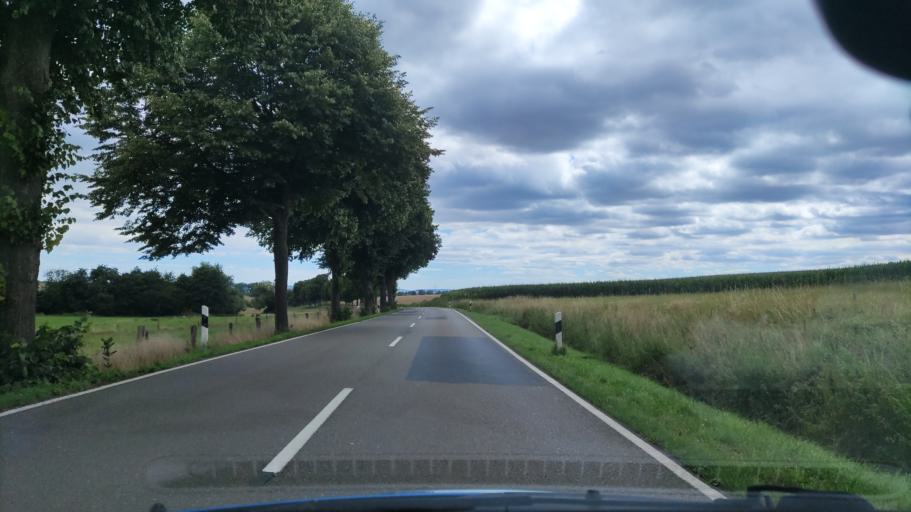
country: DE
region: Lower Saxony
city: Eimen
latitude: 51.8314
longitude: 9.8002
